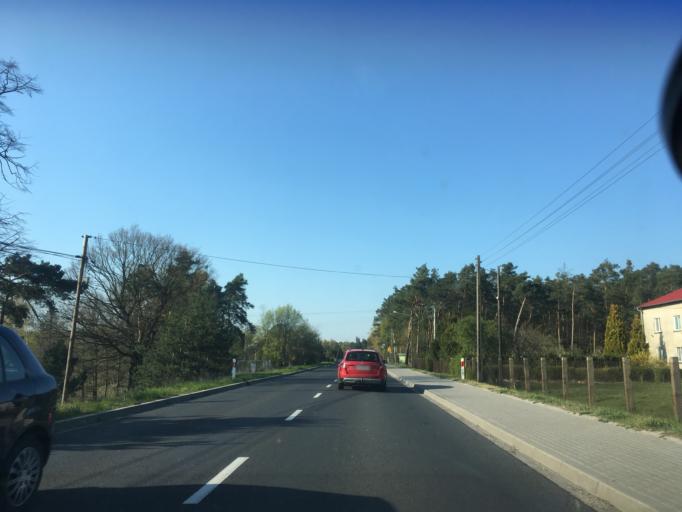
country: PL
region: Lubusz
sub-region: Powiat zaganski
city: Szprotawa
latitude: 51.4818
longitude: 15.6183
